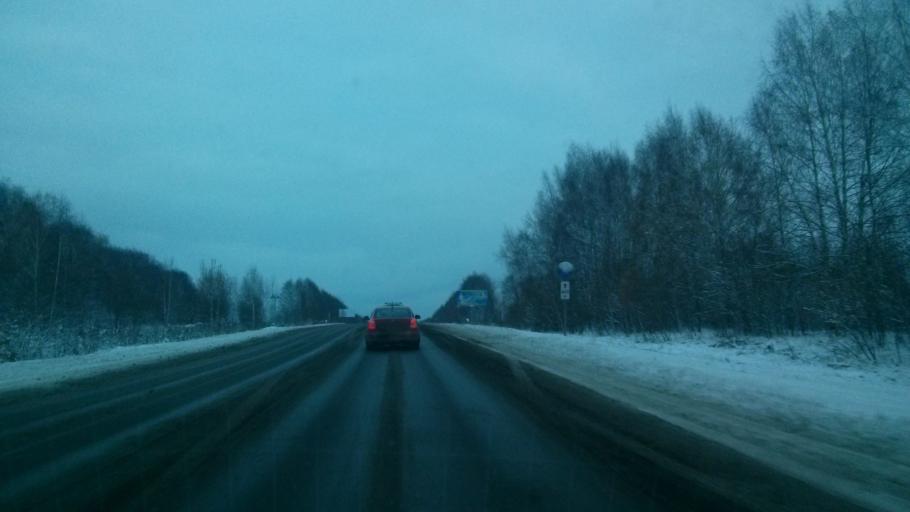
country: RU
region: Nizjnij Novgorod
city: Bogorodsk
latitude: 56.0871
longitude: 43.5304
